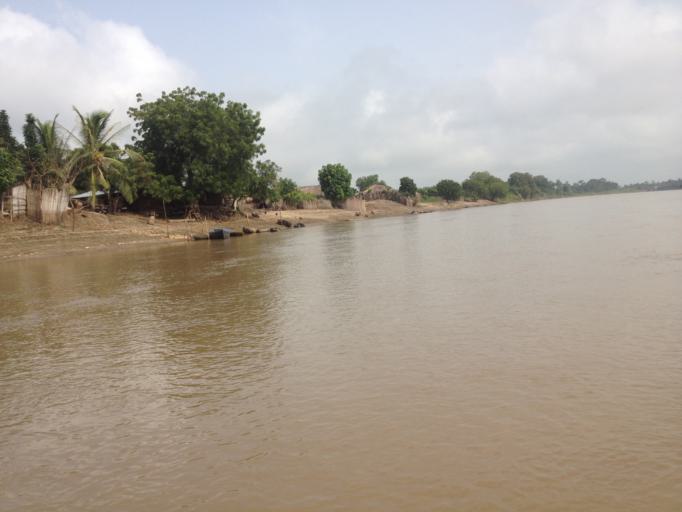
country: BJ
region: Mono
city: Grand-Popo
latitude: 6.3713
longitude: 1.7817
